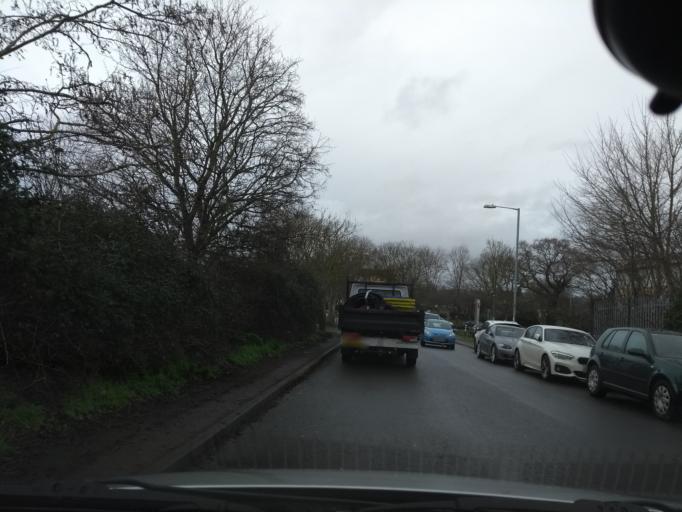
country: GB
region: England
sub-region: Somerset
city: Taunton
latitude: 51.0275
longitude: -3.0869
